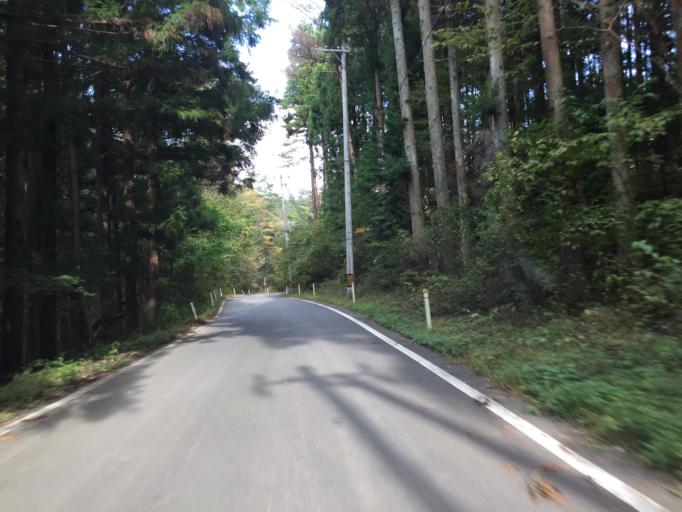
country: JP
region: Miyagi
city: Marumori
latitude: 37.8230
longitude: 140.8008
